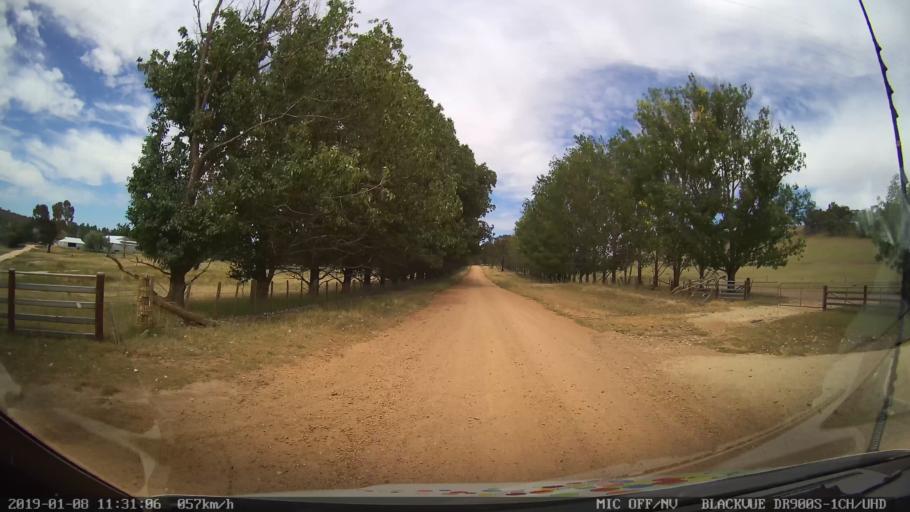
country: AU
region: New South Wales
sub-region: Guyra
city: Guyra
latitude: -30.3109
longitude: 151.5399
